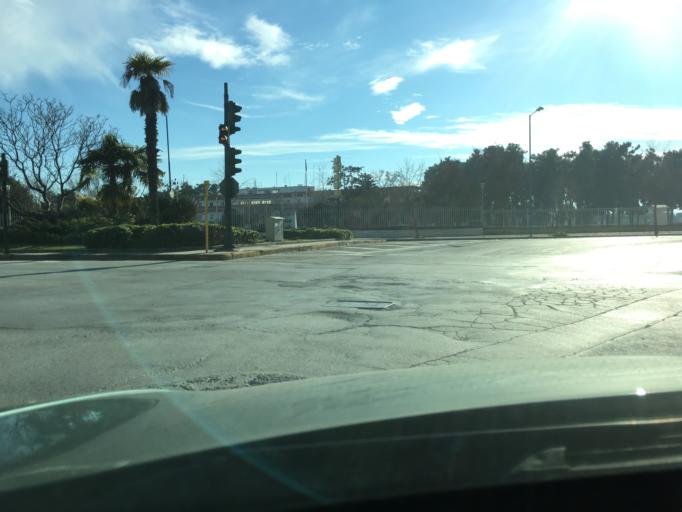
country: GR
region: Thessaly
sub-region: Nomos Larisis
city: Larisa
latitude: 39.6332
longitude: 22.4071
